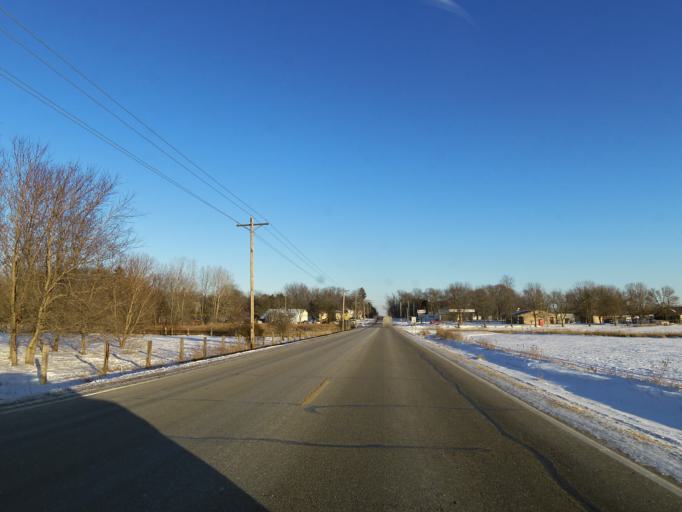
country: US
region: Minnesota
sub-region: Rice County
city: Northfield
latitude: 44.5437
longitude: -93.1592
